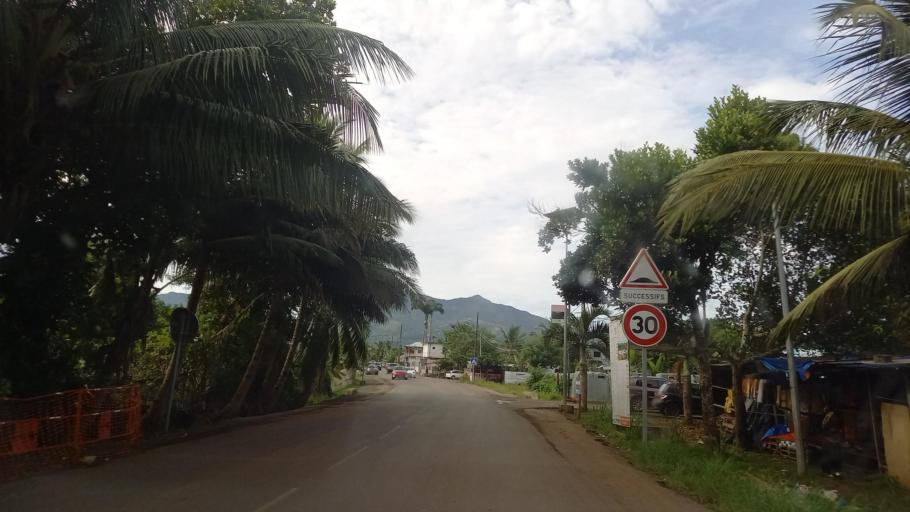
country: YT
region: Chirongui
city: Chirongui
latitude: -12.9313
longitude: 45.1526
